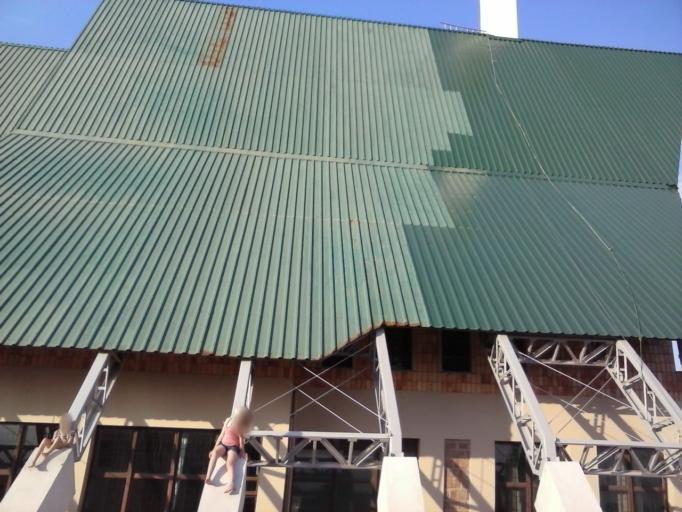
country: BR
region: Rio Grande do Sul
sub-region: Porto Alegre
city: Porto Alegre
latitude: -30.1000
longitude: -51.1820
